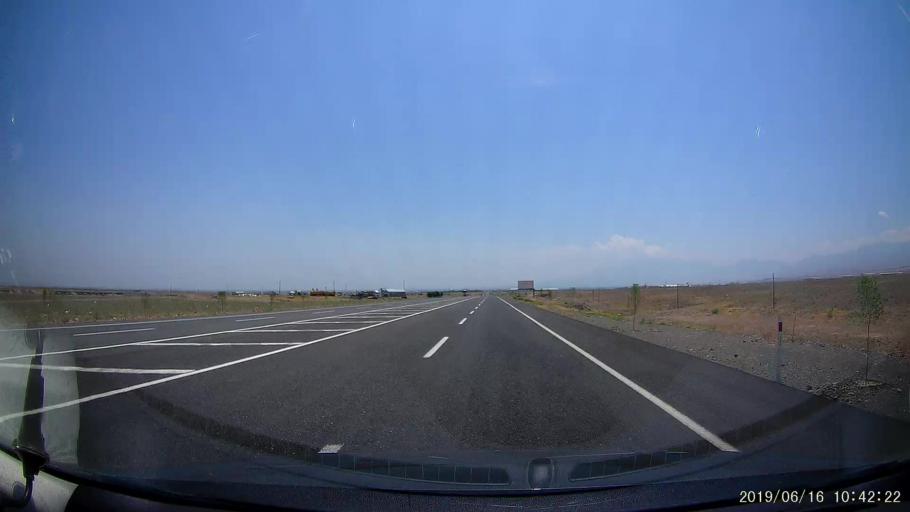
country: AM
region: Armavir
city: Shenavan
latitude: 40.0426
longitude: 43.8051
